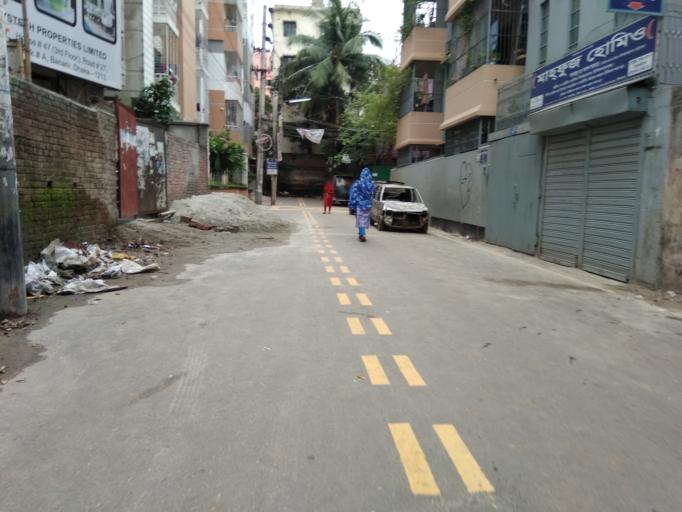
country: BD
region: Dhaka
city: Tungi
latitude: 23.8175
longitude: 90.3606
